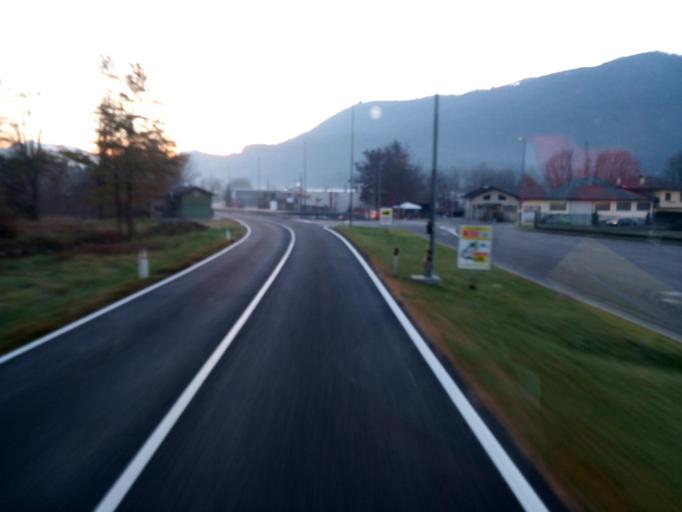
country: IT
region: Friuli Venezia Giulia
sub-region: Provincia di Udine
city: Villa Santina
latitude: 46.4140
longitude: 12.9325
